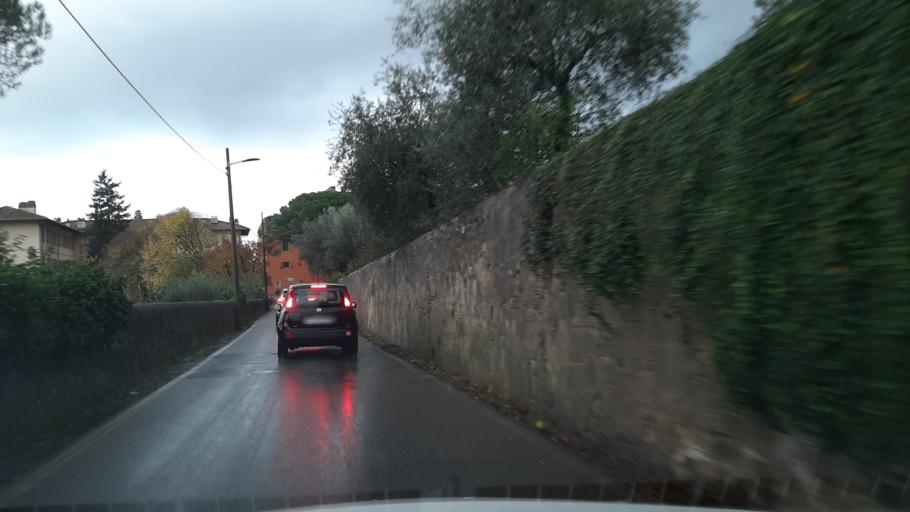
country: IT
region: Tuscany
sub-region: Province of Florence
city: Florence
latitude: 43.8124
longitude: 11.2521
